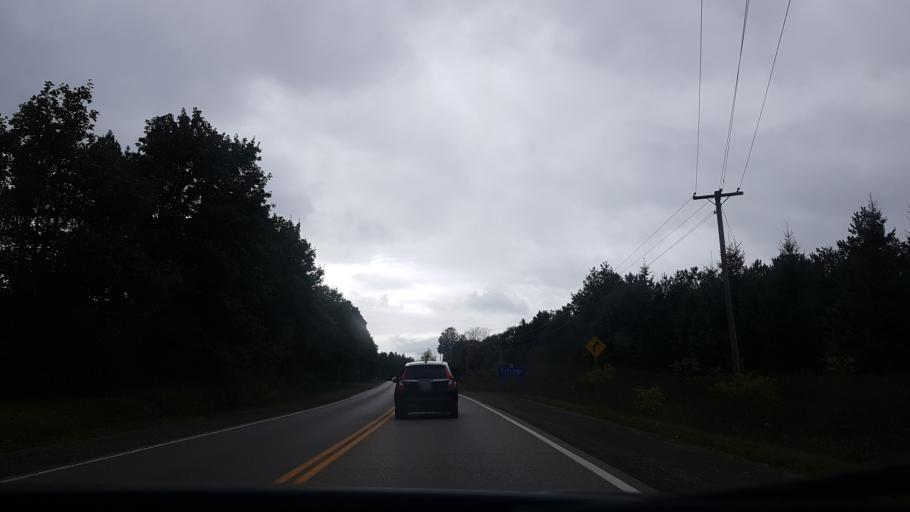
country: CA
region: Ontario
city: Uxbridge
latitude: 44.1040
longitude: -79.0941
